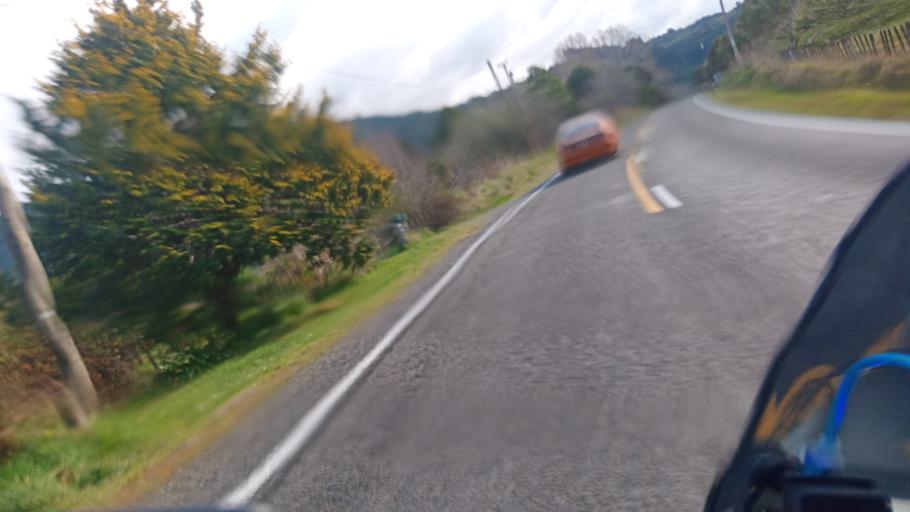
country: NZ
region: Gisborne
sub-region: Gisborne District
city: Gisborne
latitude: -38.1156
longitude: 178.2966
